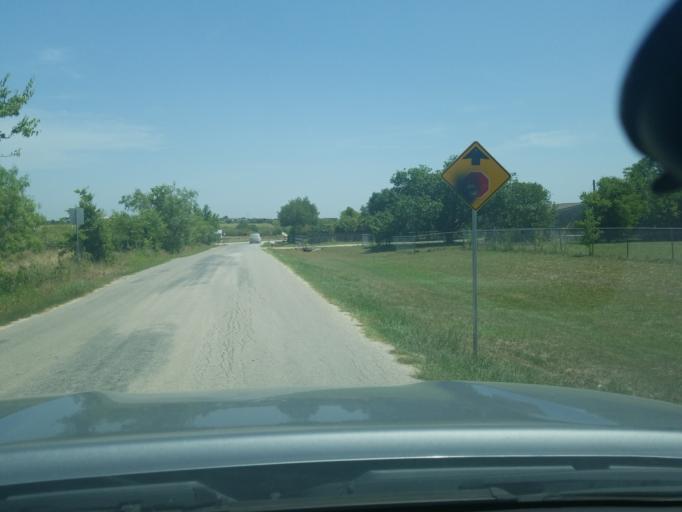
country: US
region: Texas
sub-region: Guadalupe County
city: Cibolo
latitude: 29.5715
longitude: -98.1925
